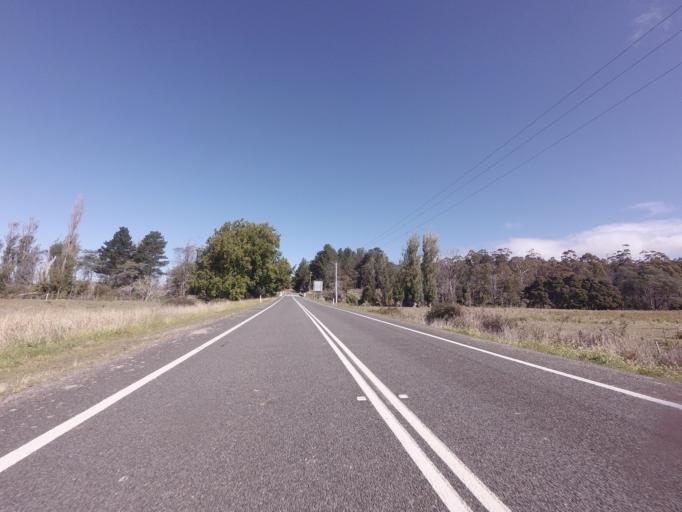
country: AU
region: Tasmania
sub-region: Break O'Day
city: St Helens
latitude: -41.6657
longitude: 148.2841
